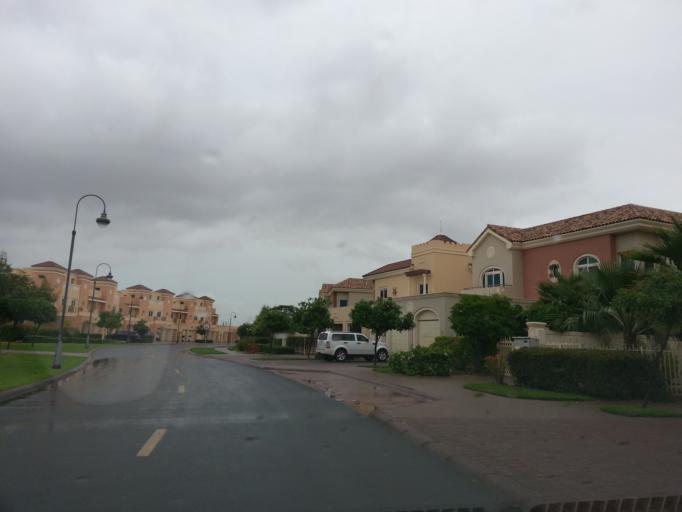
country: AE
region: Dubai
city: Dubai
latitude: 25.0316
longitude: 55.2085
